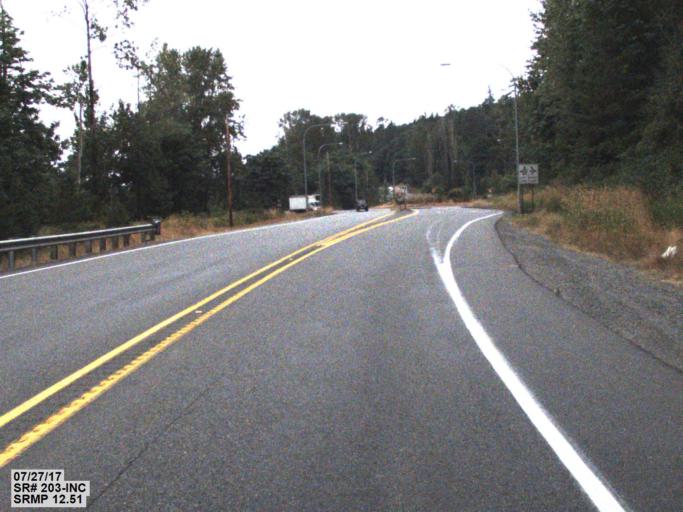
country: US
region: Washington
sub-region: King County
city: Duvall
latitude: 47.7075
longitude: -121.9846
